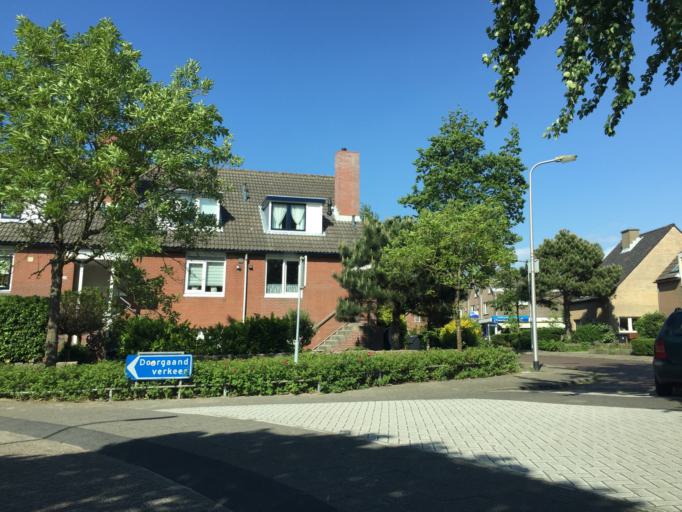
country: NL
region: South Holland
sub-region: Gemeente Noordwijkerhout
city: Noordwijkerhout
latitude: 52.2601
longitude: 4.4887
